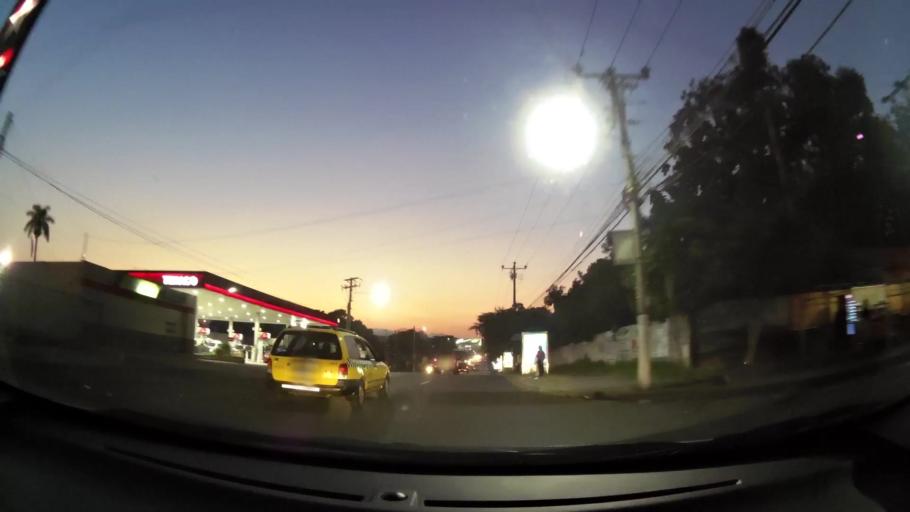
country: SV
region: La Libertad
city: Antiguo Cuscatlan
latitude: 13.6809
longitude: -89.2480
